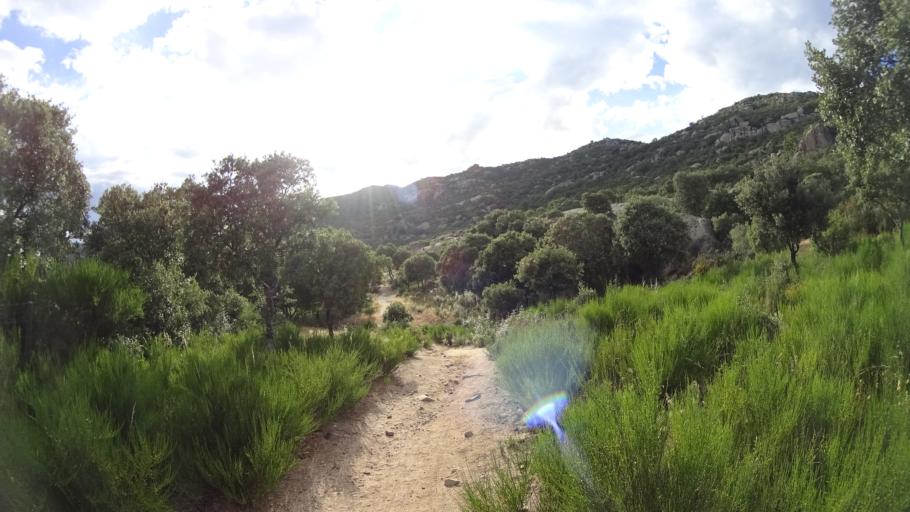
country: ES
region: Madrid
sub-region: Provincia de Madrid
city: Hoyo de Manzanares
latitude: 40.6348
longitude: -3.9015
